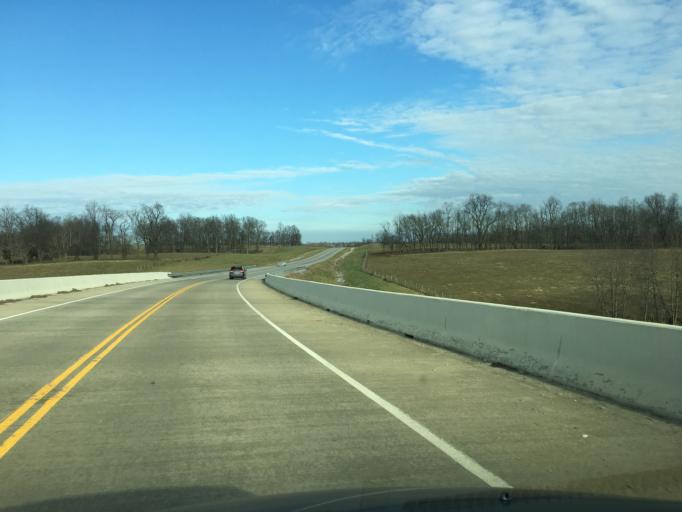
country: US
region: Kentucky
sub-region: Scott County
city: Georgetown
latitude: 38.2190
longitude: -84.5938
